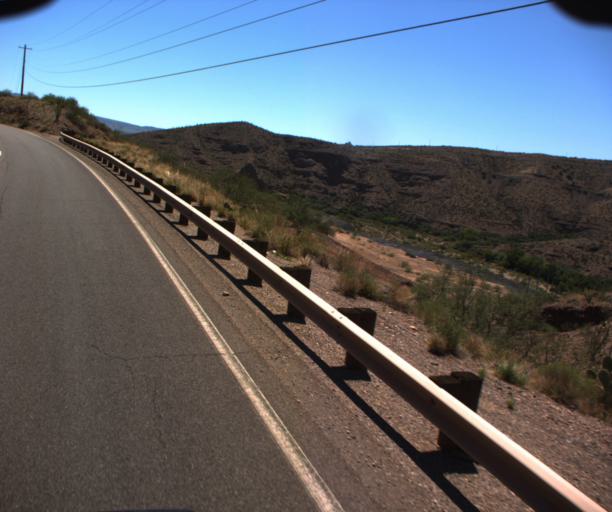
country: US
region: Arizona
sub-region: Greenlee County
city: Clifton
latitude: 33.0320
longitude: -109.2992
